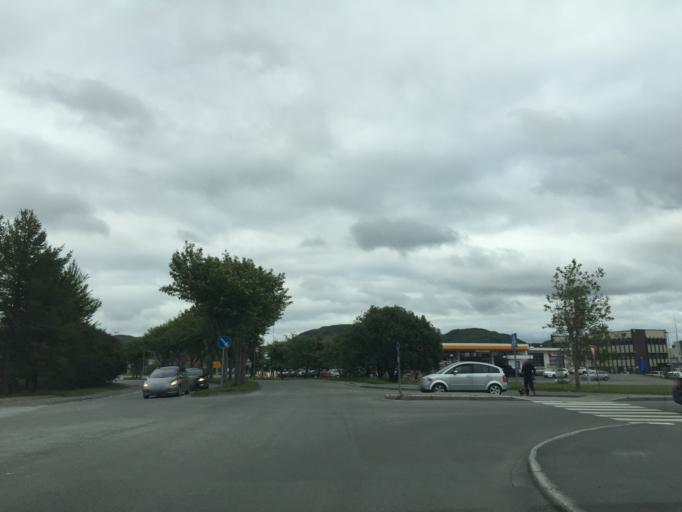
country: NO
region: Nordland
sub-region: Bodo
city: Bodo
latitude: 67.2800
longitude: 14.4182
